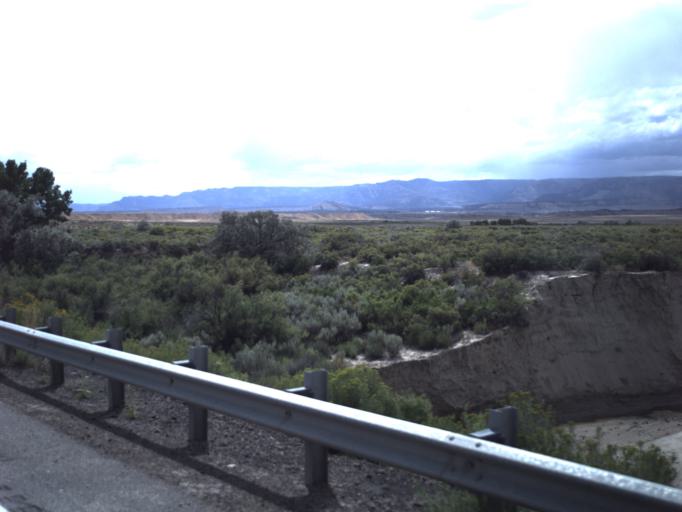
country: US
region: Utah
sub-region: Carbon County
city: Price
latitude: 39.5233
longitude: -110.8243
